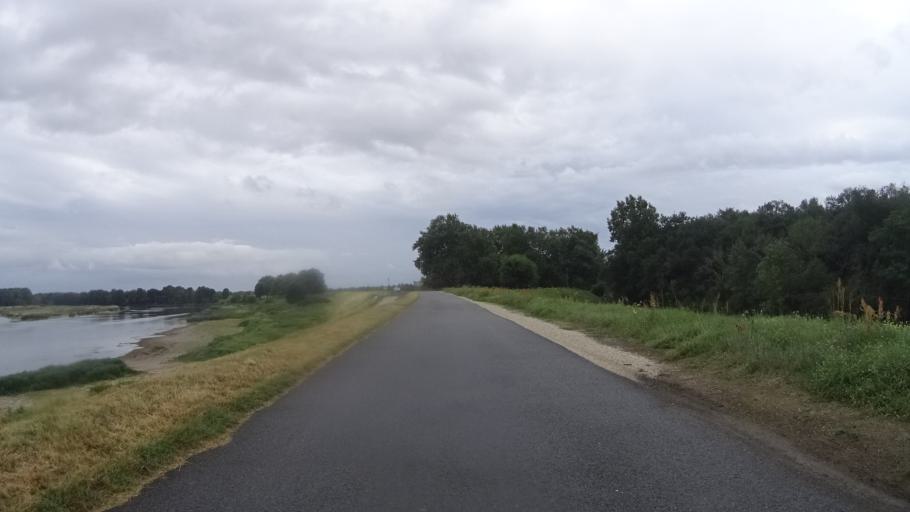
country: FR
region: Centre
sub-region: Departement du Loiret
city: Sandillon
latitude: 47.8547
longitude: 2.0340
